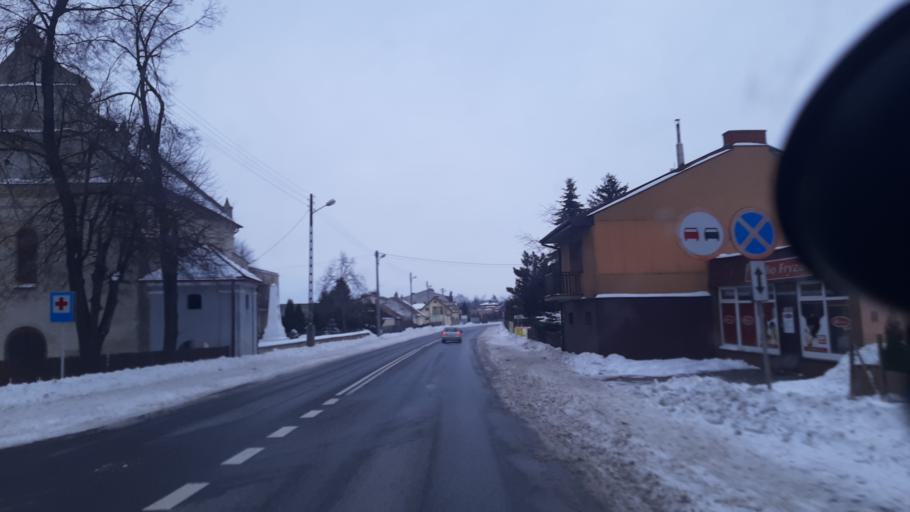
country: PL
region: Lublin Voivodeship
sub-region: Powiat pulawski
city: Markuszow
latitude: 51.3742
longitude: 22.2621
